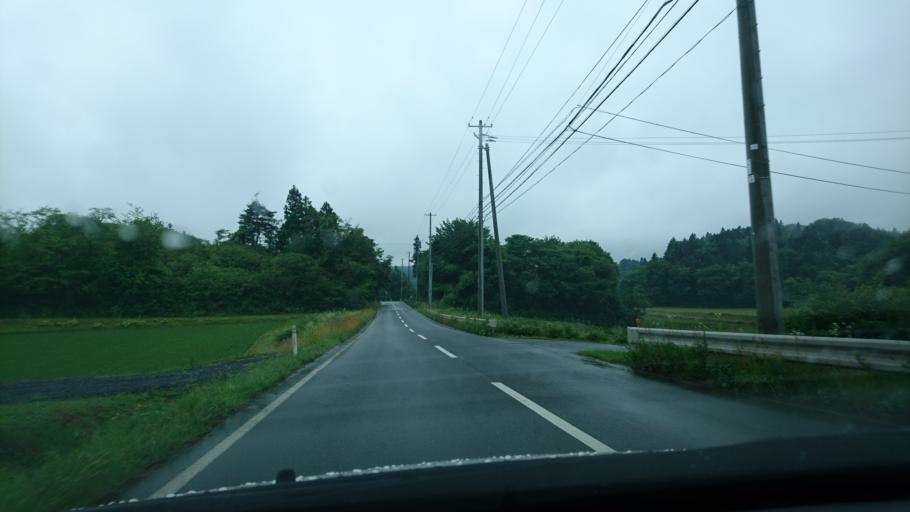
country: JP
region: Iwate
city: Ichinoseki
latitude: 38.9312
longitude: 141.0293
